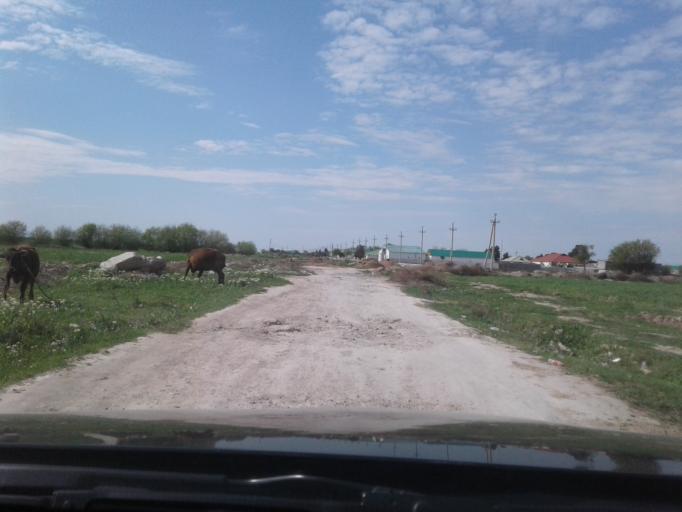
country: TM
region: Ahal
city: Ashgabat
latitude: 37.9799
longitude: 58.2900
